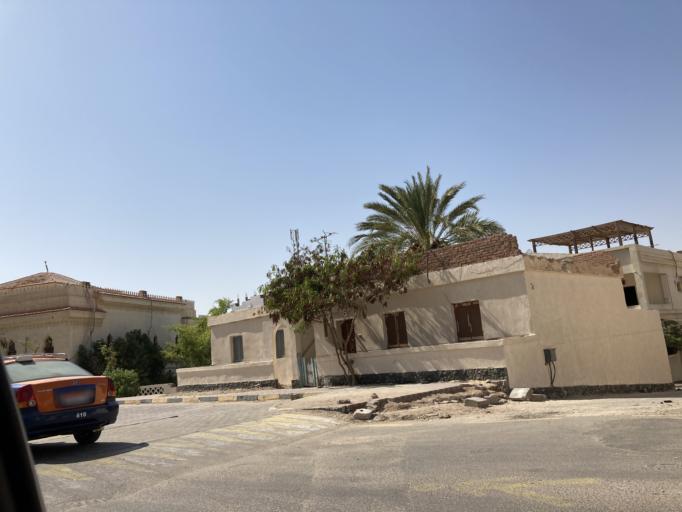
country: EG
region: Red Sea
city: Hurghada
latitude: 27.2547
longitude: 33.8288
